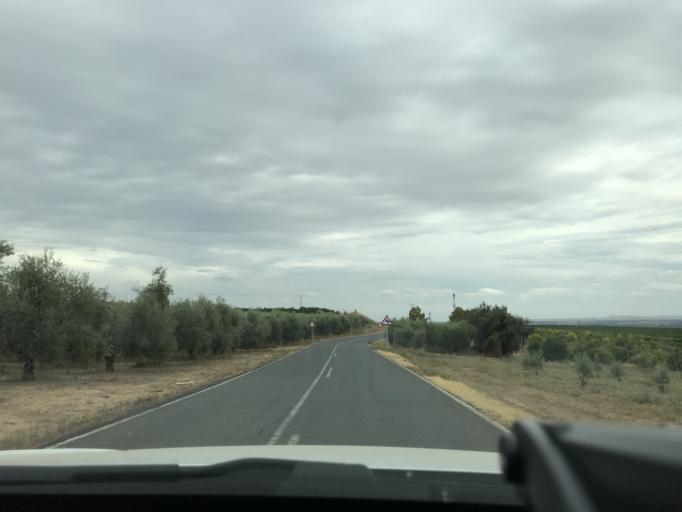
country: ES
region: Andalusia
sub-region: Provincia de Sevilla
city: Villanueva del Rio y Minas
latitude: 37.6430
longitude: -5.7067
